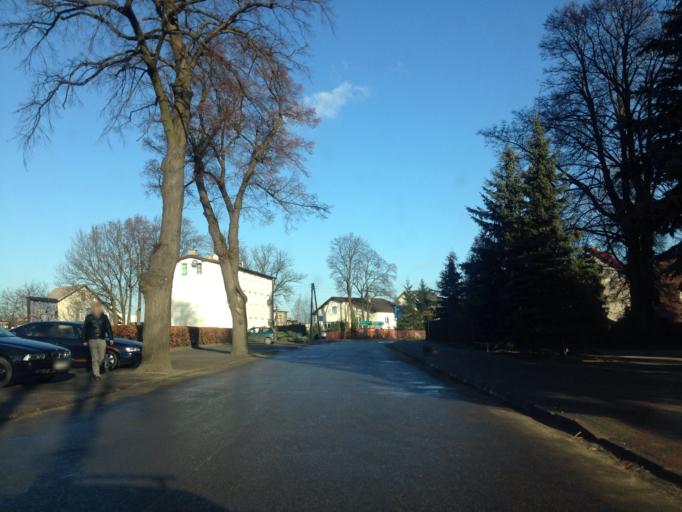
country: PL
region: Kujawsko-Pomorskie
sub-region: Powiat brodnicki
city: Jablonowo Pomorskie
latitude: 53.3945
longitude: 19.1566
